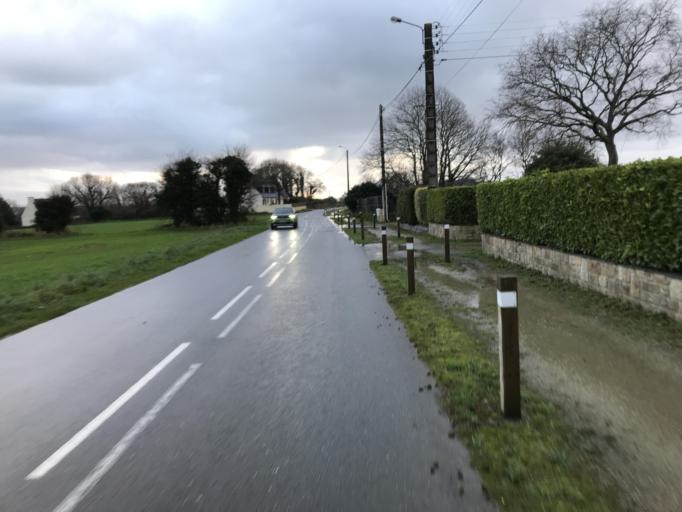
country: FR
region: Brittany
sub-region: Departement du Finistere
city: Loperhet
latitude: 48.3744
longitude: -4.3160
